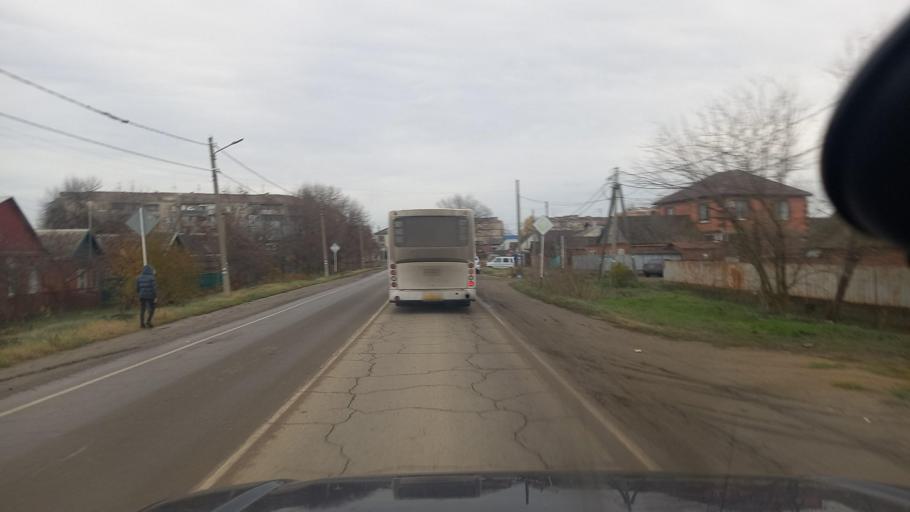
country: RU
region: Adygeya
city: Yablonovskiy
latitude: 44.9801
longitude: 38.9321
